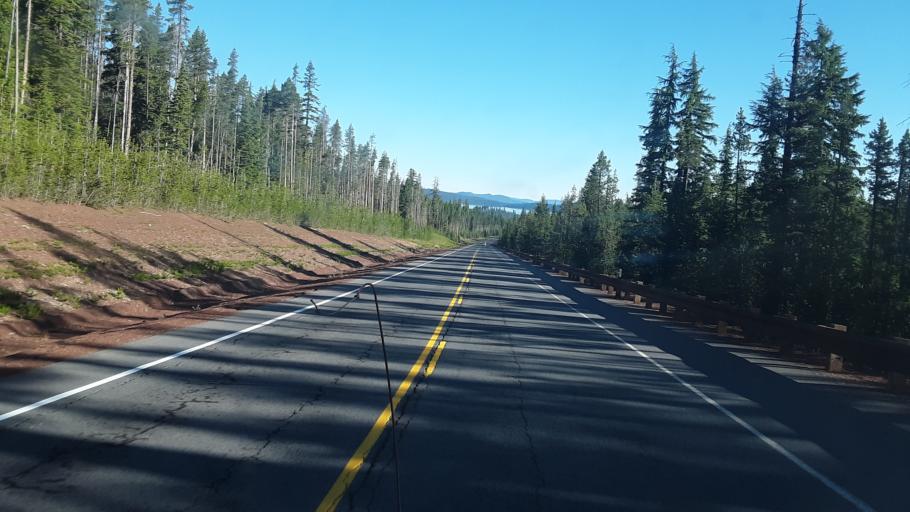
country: US
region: Oregon
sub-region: Lane County
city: Oakridge
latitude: 43.1073
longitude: -122.1296
